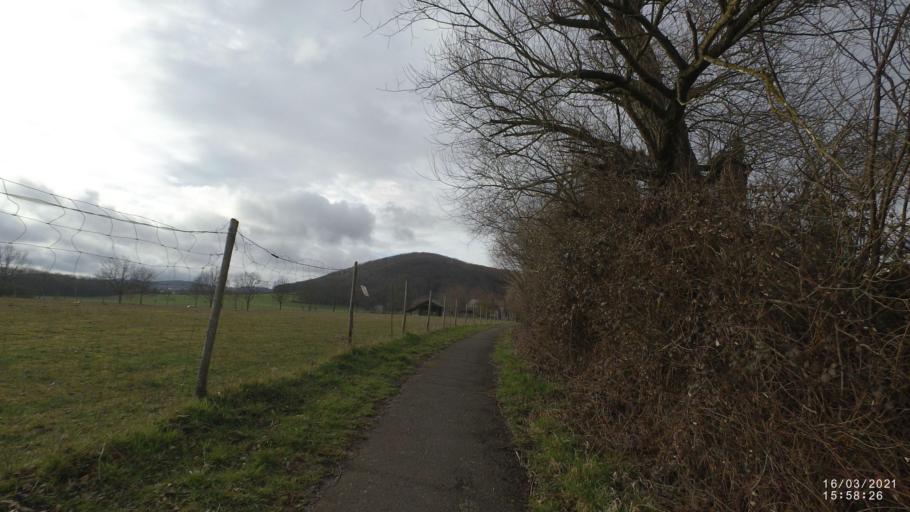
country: DE
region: Rheinland-Pfalz
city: Mendig
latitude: 50.3877
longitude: 7.2710
